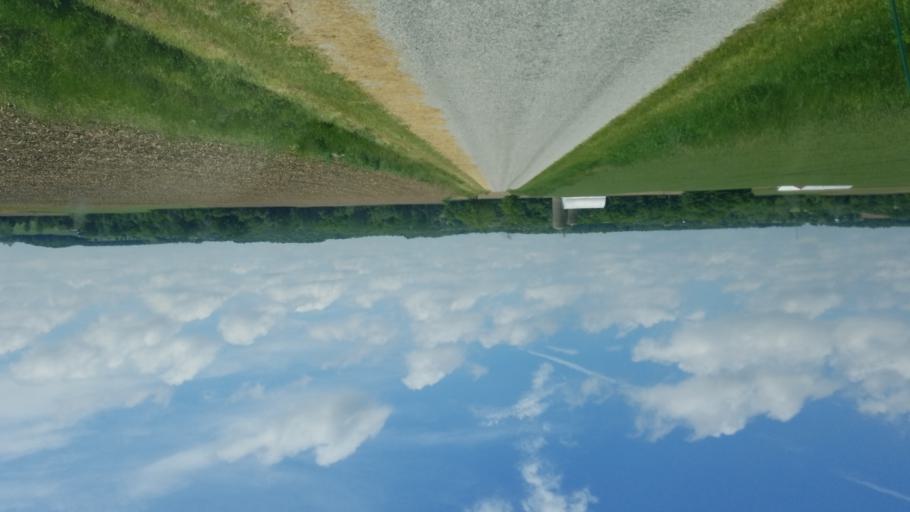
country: US
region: Ohio
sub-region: Wayne County
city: West Salem
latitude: 40.8430
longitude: -82.1505
